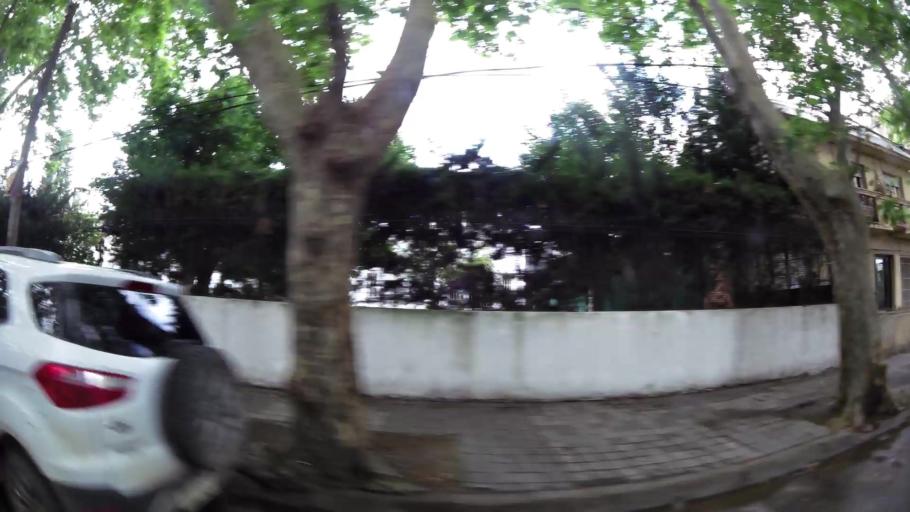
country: UY
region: Montevideo
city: Montevideo
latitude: -34.8705
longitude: -56.1860
